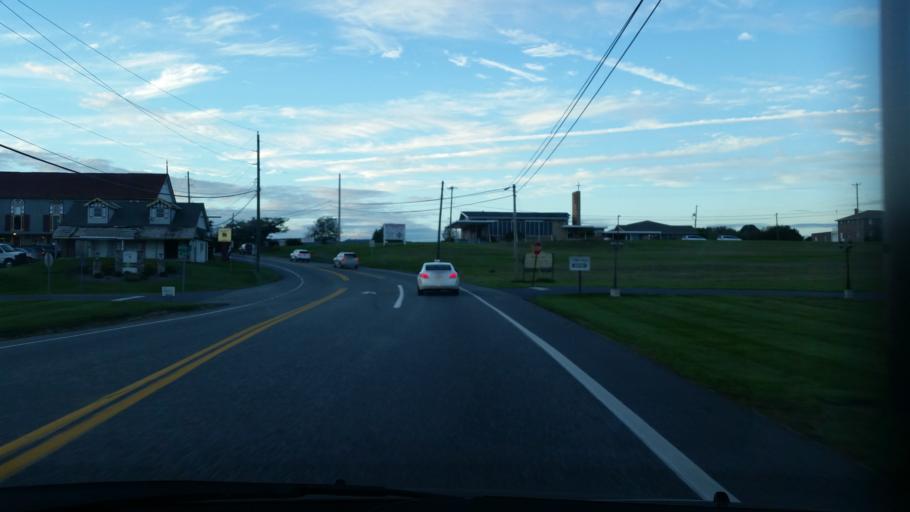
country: US
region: Pennsylvania
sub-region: Dauphin County
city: Palmdale
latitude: 40.3724
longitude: -76.6507
